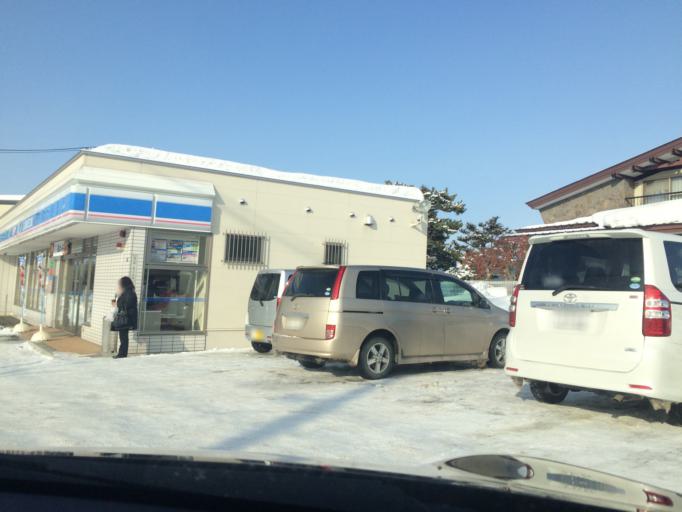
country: JP
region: Hokkaido
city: Ebetsu
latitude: 43.0398
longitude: 141.4888
